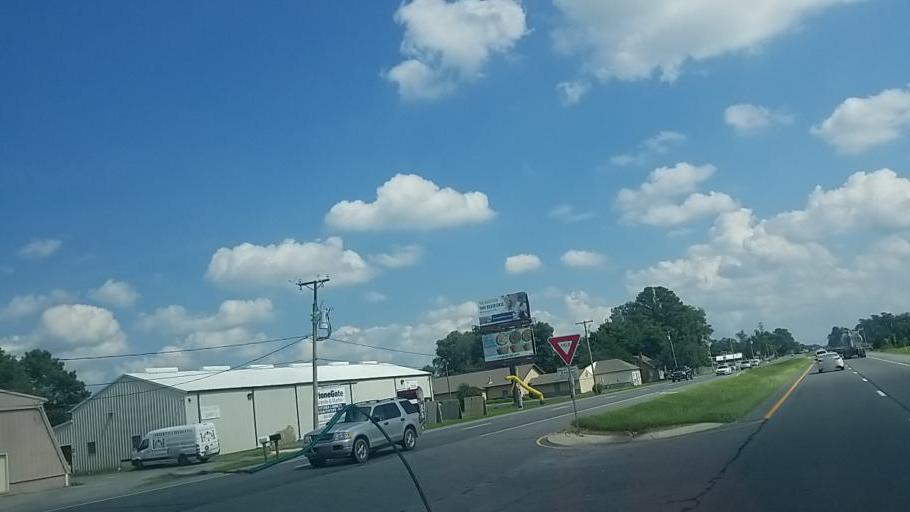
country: US
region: Delaware
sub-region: Sussex County
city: Georgetown
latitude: 38.6375
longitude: -75.3535
